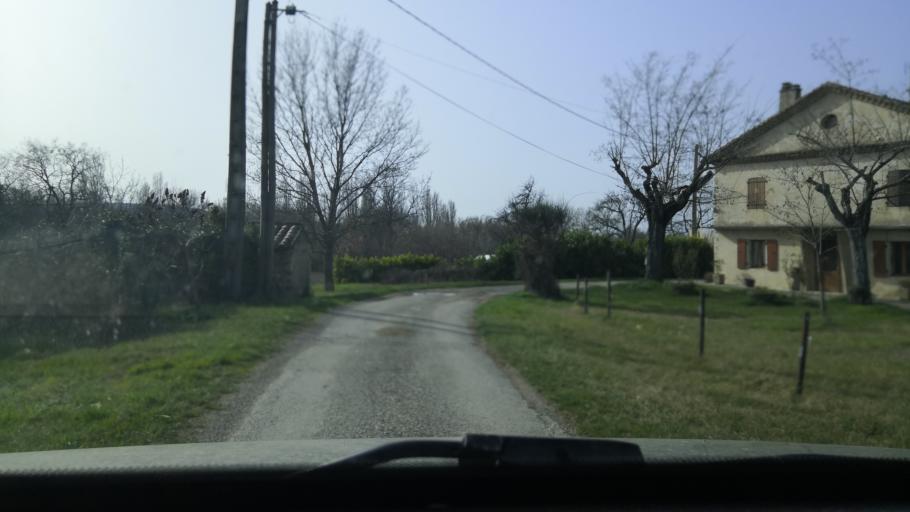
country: FR
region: Rhone-Alpes
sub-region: Departement de la Drome
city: La Begude-de-Mazenc
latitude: 44.5404
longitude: 4.9150
